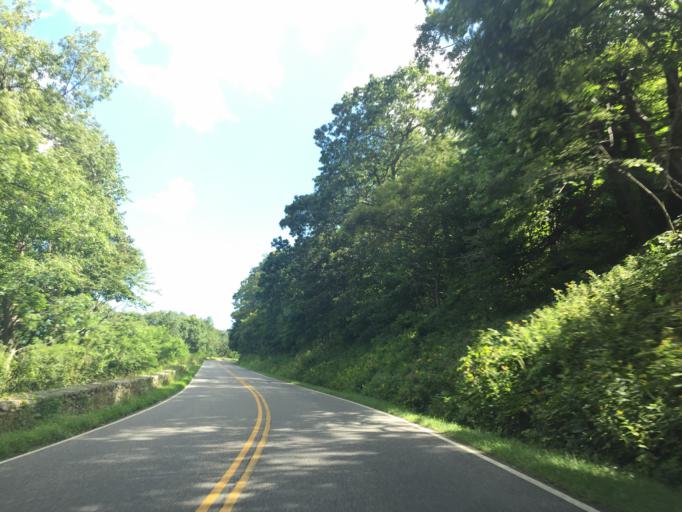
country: US
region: Virginia
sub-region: Page County
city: Luray
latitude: 38.6326
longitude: -78.3226
